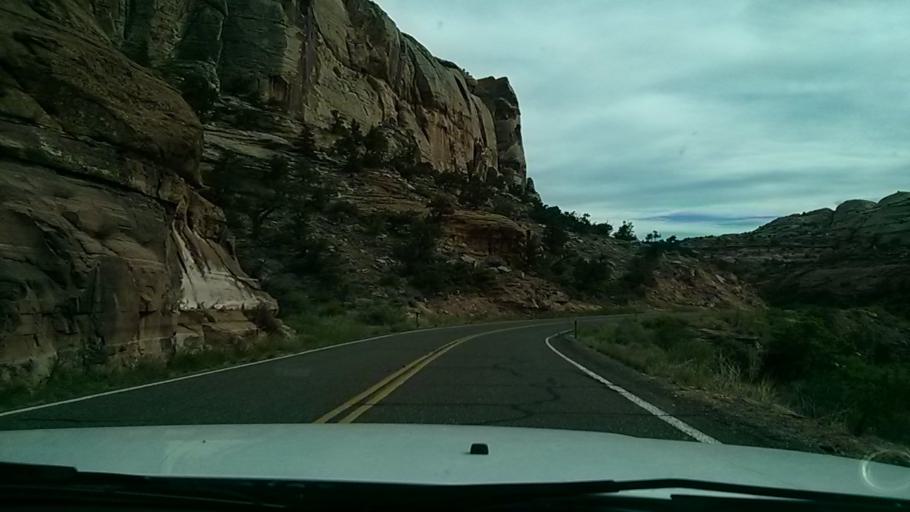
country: US
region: Utah
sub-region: Wayne County
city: Loa
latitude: 37.7897
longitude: -111.4157
